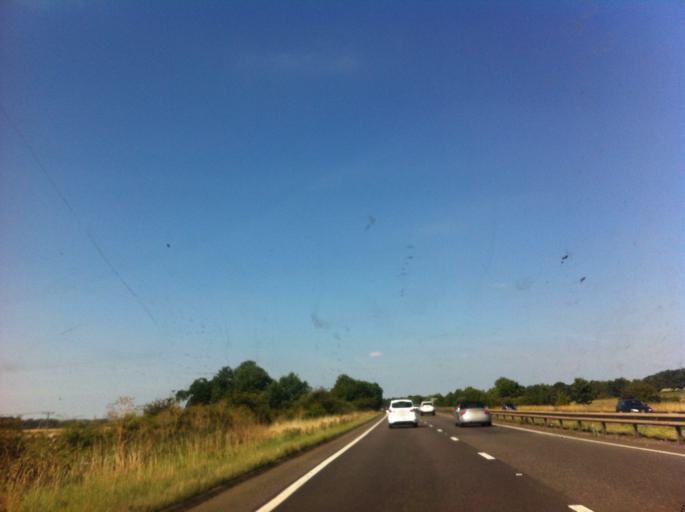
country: GB
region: England
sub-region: Northamptonshire
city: Earls Barton
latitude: 52.2551
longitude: -0.7667
